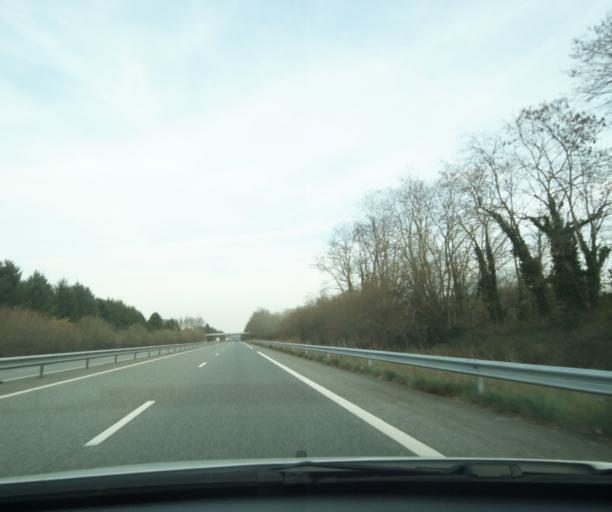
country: FR
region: Midi-Pyrenees
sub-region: Departement des Hautes-Pyrenees
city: Laloubere
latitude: 43.2107
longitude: 0.0634
